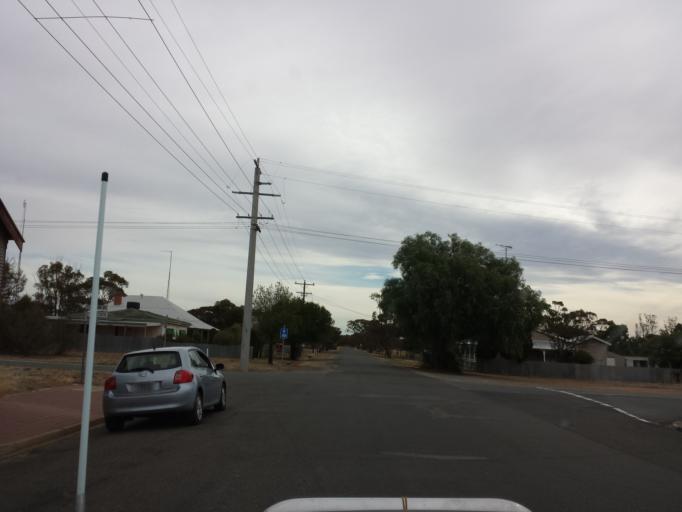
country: AU
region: Victoria
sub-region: Horsham
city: Horsham
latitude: -36.0762
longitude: 142.4145
